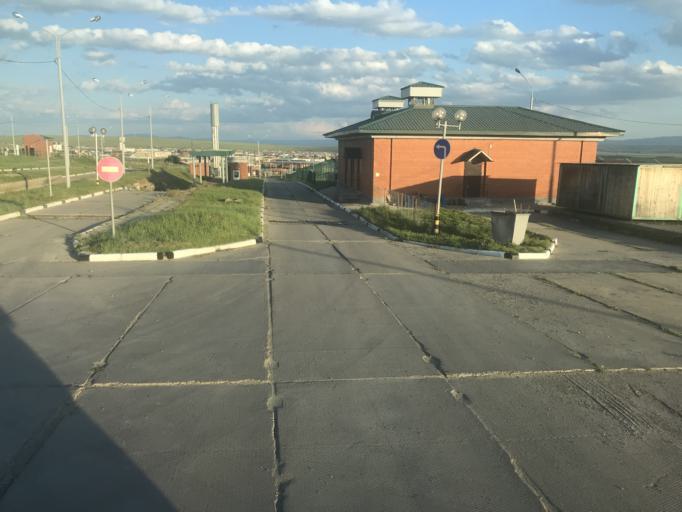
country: MN
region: Selenge
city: Altanbulag
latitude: 50.3250
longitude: 106.4876
